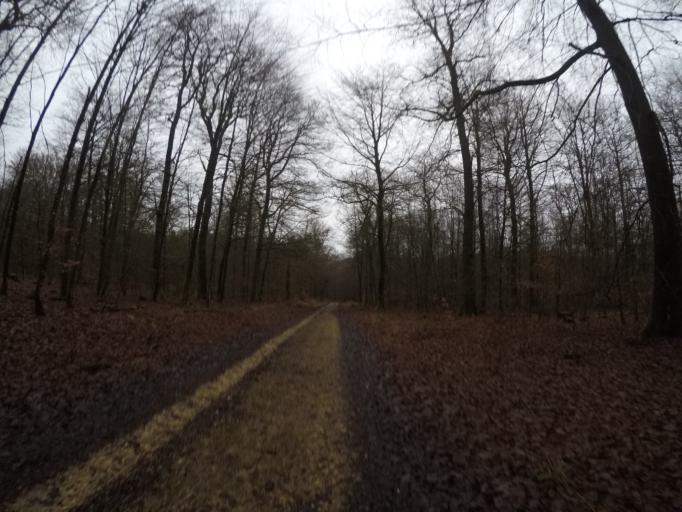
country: BE
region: Wallonia
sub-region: Province du Luxembourg
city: Fauvillers
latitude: 49.8135
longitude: 5.6410
